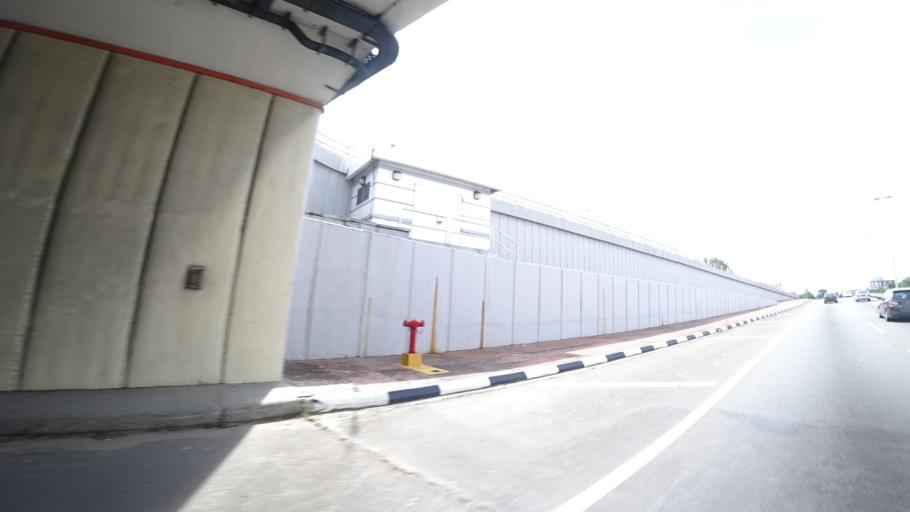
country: BN
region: Brunei and Muara
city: Bandar Seri Begawan
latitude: 4.9016
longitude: 114.9195
